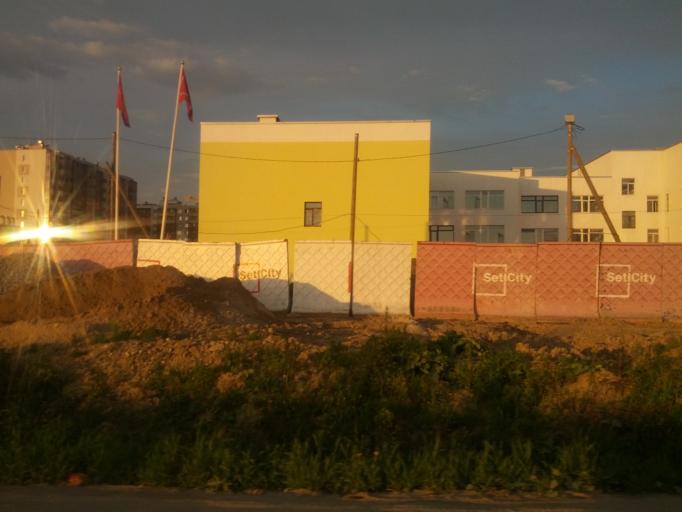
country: RU
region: Leningrad
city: Rybatskoye
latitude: 59.8994
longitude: 30.5051
